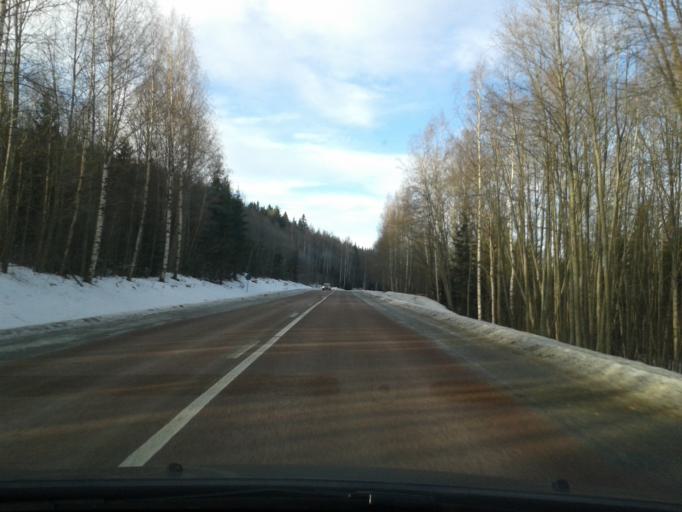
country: SE
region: Vaesternorrland
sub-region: OErnskoeldsviks Kommun
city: Bjasta
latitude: 63.3417
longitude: 18.5054
